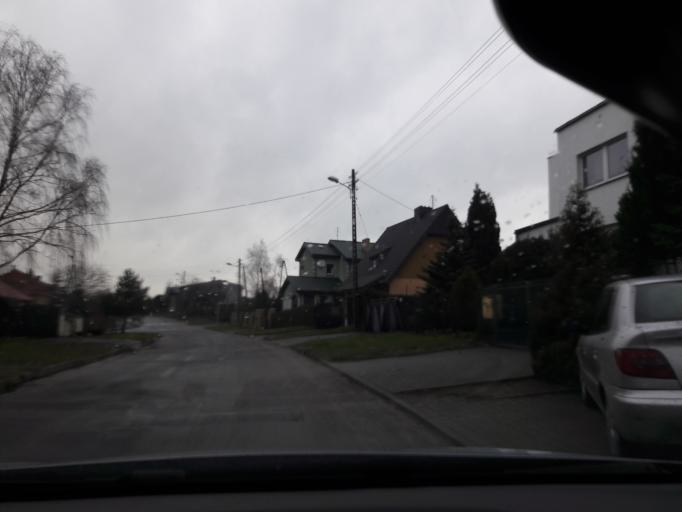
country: PL
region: Greater Poland Voivodeship
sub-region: Powiat poznanski
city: Suchy Las
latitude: 52.4835
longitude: 16.8857
